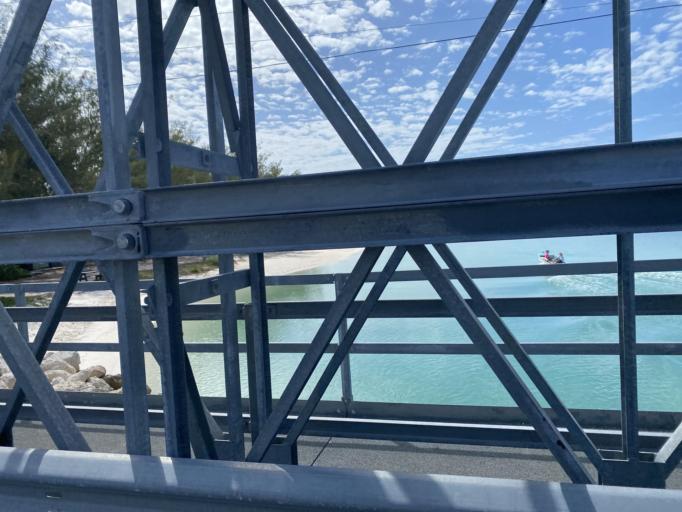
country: BS
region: Spanish Wells
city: Spanish Wells
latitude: 25.5476
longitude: -76.7714
